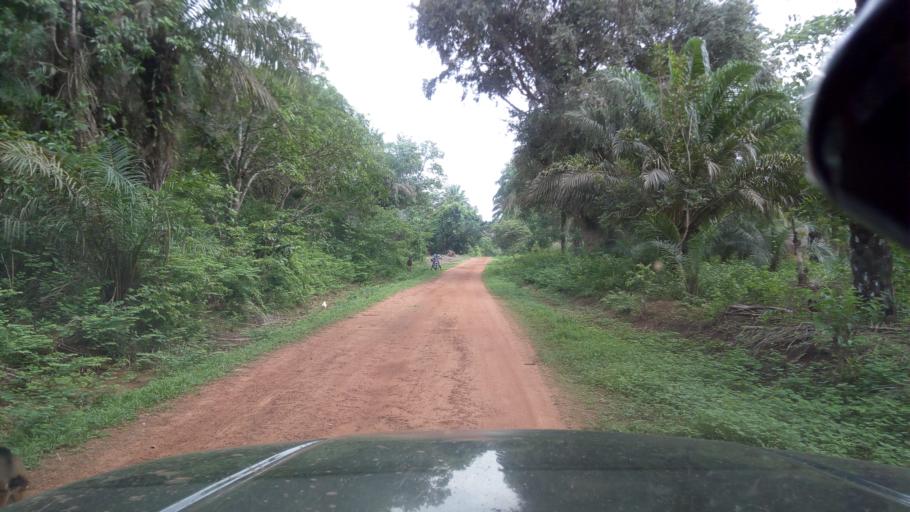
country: SL
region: Northern Province
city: Mange
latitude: 8.8099
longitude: -12.9284
